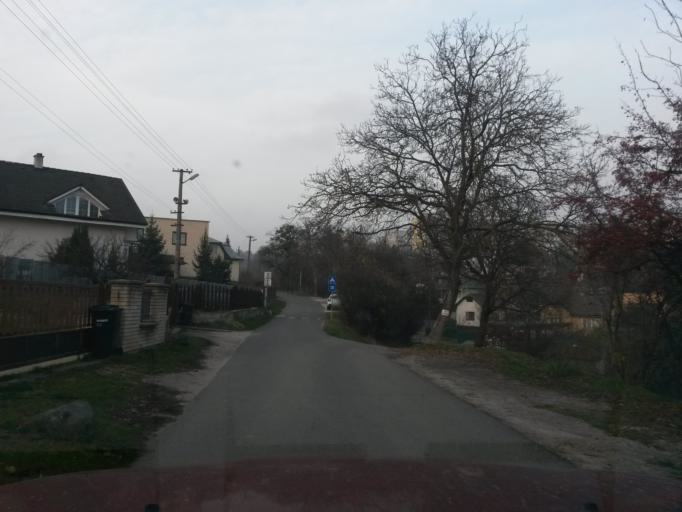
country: SK
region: Kosicky
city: Kosice
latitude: 48.7136
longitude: 21.2047
